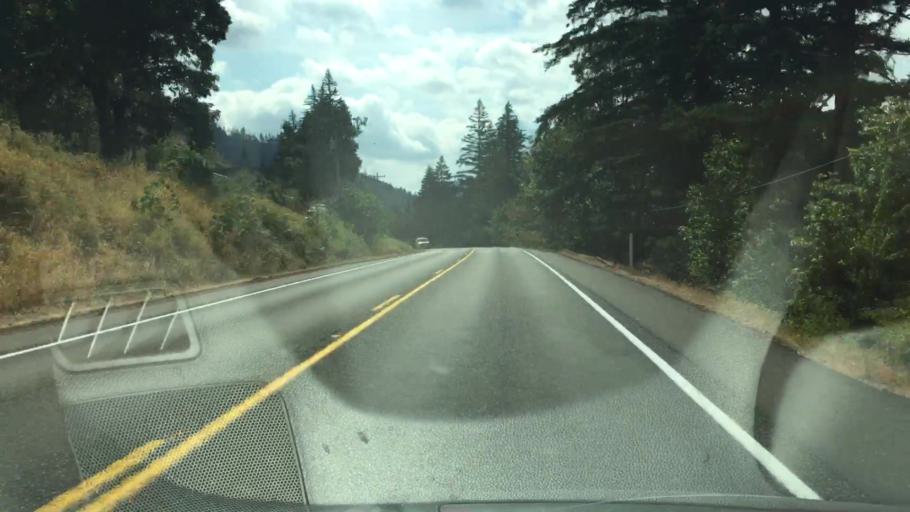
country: US
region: Washington
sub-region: Klickitat County
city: White Salmon
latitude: 45.7837
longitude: -121.5045
